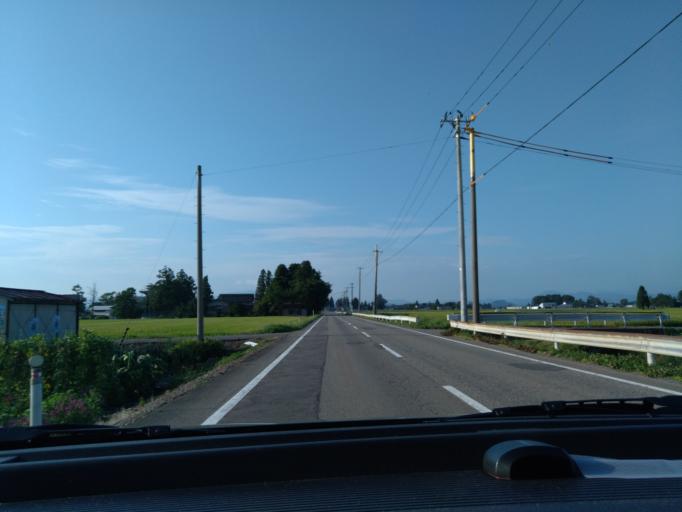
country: JP
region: Akita
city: Kakunodatemachi
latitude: 39.5217
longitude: 140.5582
